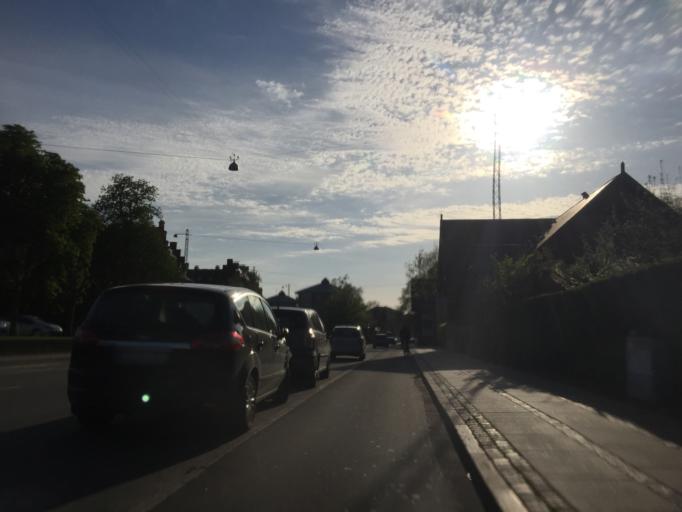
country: DK
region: Capital Region
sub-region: Frederiksberg Kommune
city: Frederiksberg
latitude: 55.6793
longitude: 12.5196
